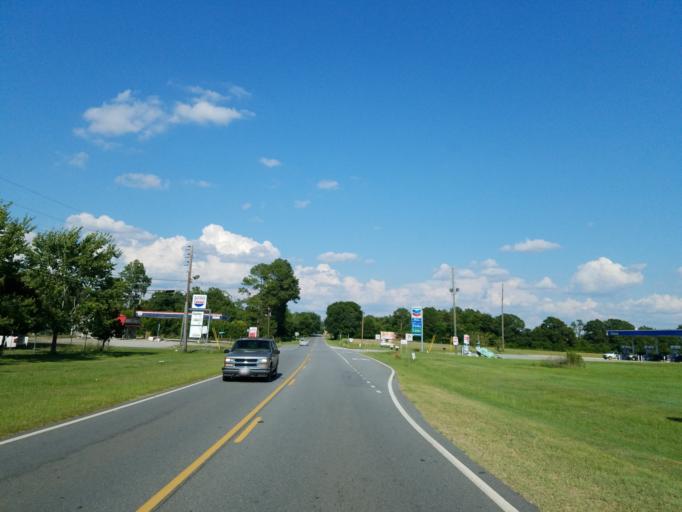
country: US
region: Georgia
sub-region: Dooly County
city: Unadilla
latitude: 32.2604
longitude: -83.7474
